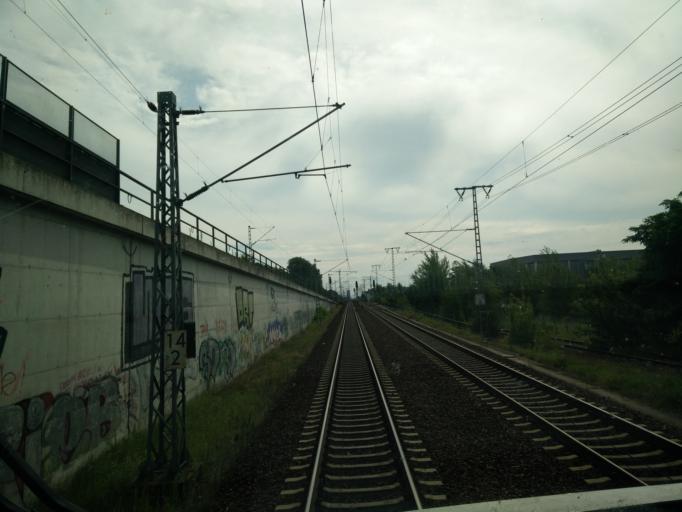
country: DE
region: Berlin
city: Falkenhagener Feld
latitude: 52.5384
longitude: 13.1726
